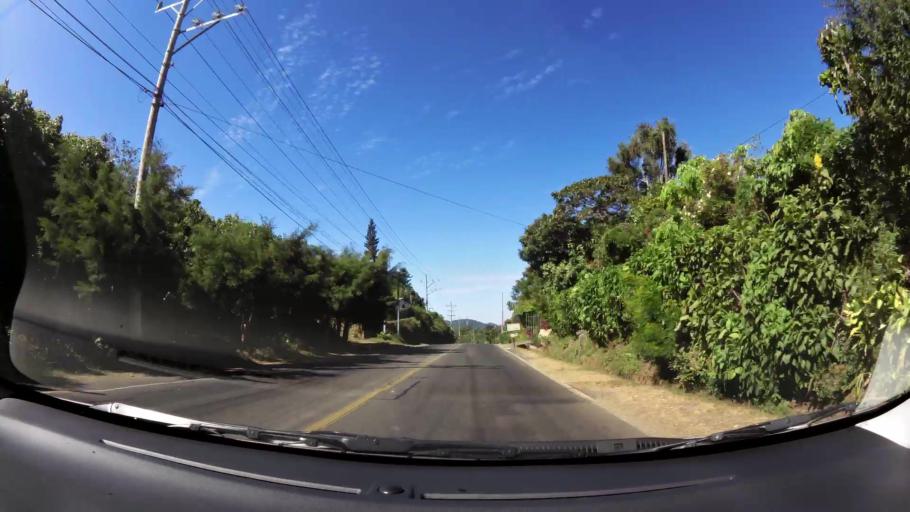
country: SV
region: Ahuachapan
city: Concepcion de Ataco
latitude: 13.8495
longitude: -89.8209
